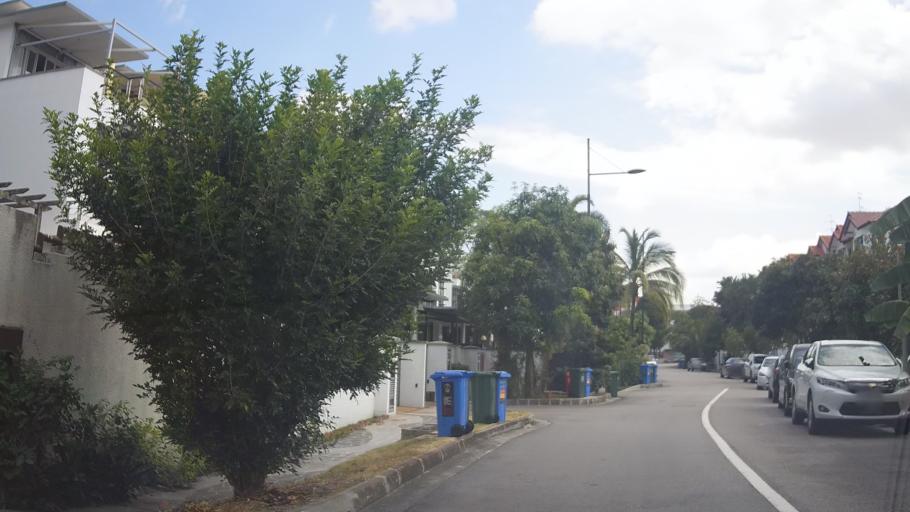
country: SG
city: Singapore
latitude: 1.3228
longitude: 103.9525
